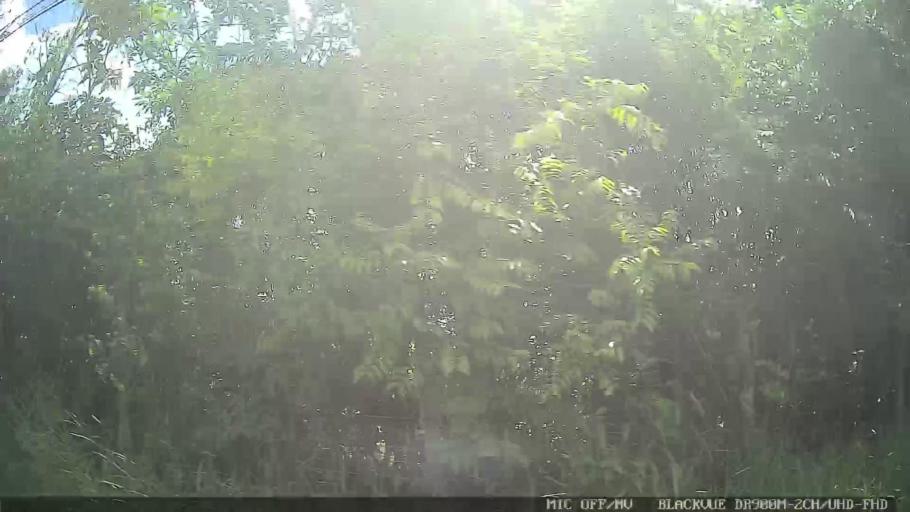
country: BR
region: Sao Paulo
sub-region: Jarinu
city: Jarinu
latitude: -23.0856
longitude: -46.6422
